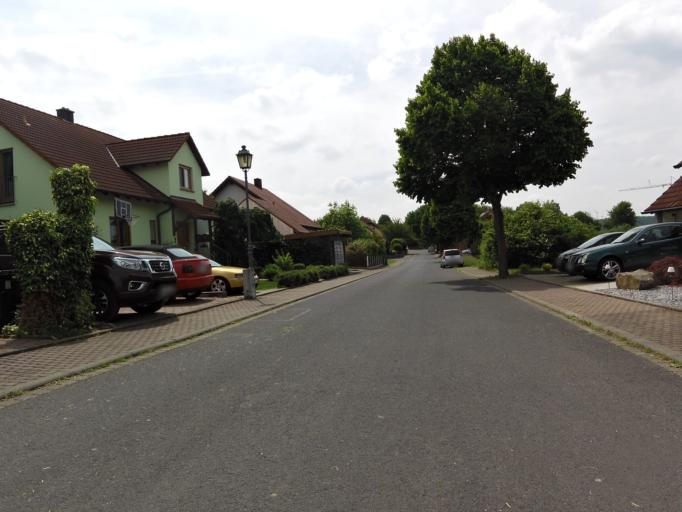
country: DE
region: Bavaria
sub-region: Regierungsbezirk Unterfranken
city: Waldbrunn
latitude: 49.7609
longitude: 9.7963
